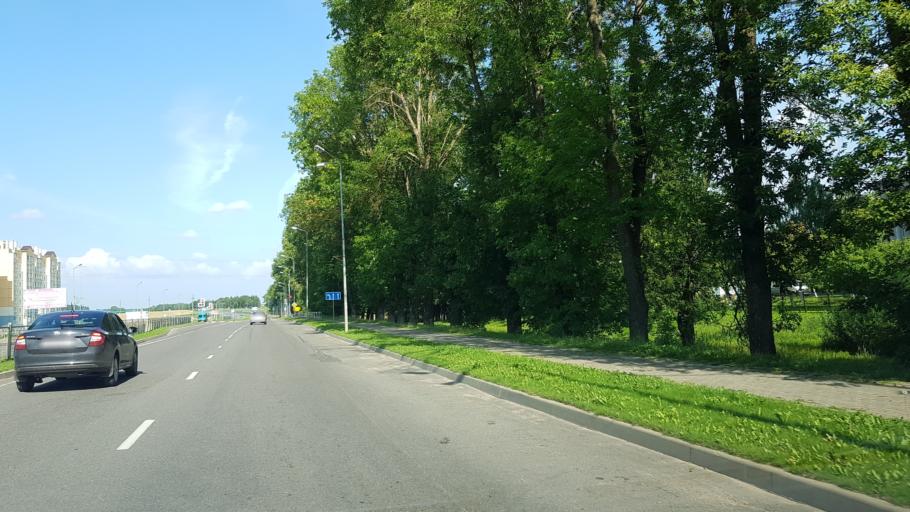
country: BY
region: Minsk
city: Dzyarzhynsk
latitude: 53.6878
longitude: 27.1562
